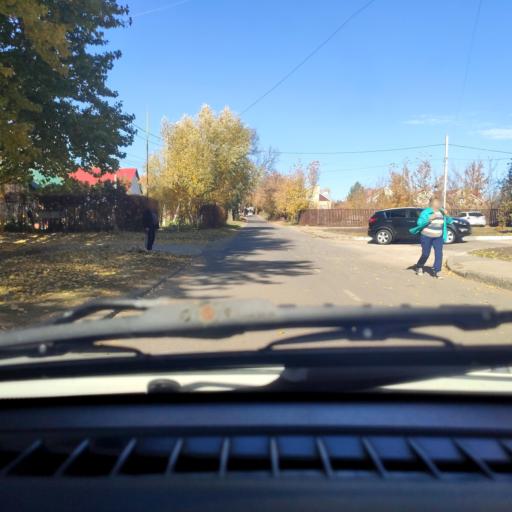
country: RU
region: Samara
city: Tol'yatti
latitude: 53.5310
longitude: 49.3896
